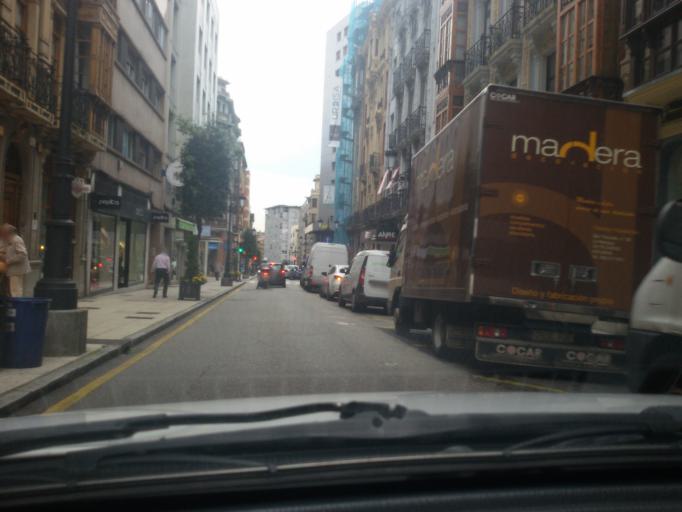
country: ES
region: Asturias
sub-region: Province of Asturias
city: Oviedo
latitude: 43.3654
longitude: -5.8527
